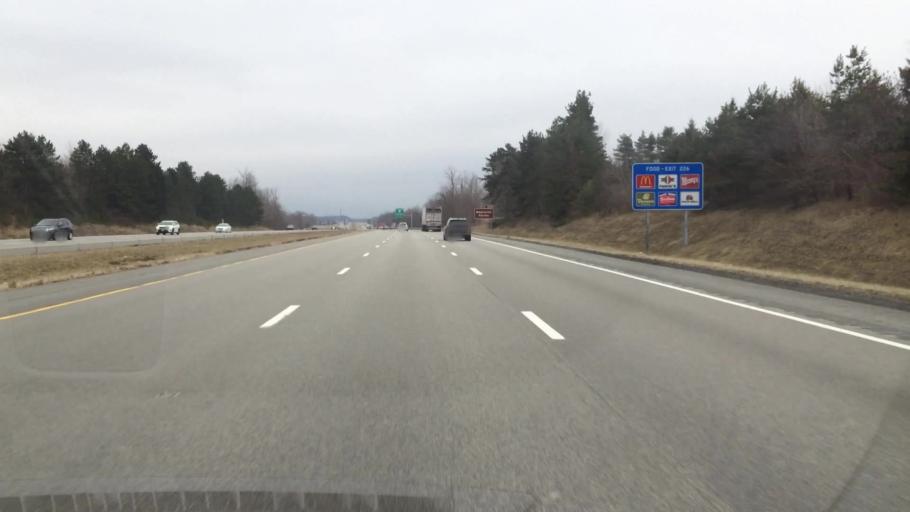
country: US
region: Ohio
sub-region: Medina County
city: Brunswick
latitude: 41.2535
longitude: -81.8035
